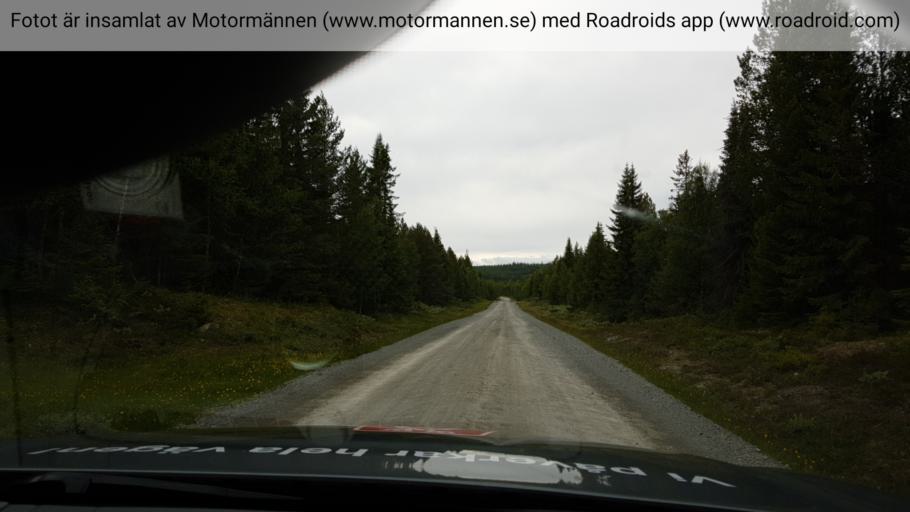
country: SE
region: Jaemtland
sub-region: Bergs Kommun
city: Hoverberg
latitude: 62.8469
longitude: 13.8489
